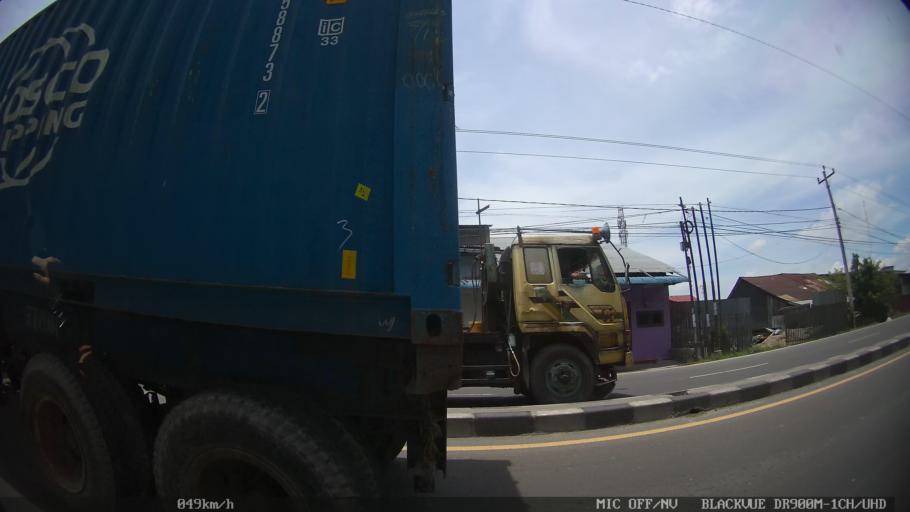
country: ID
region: North Sumatra
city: Labuhan Deli
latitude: 3.7302
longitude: 98.6759
